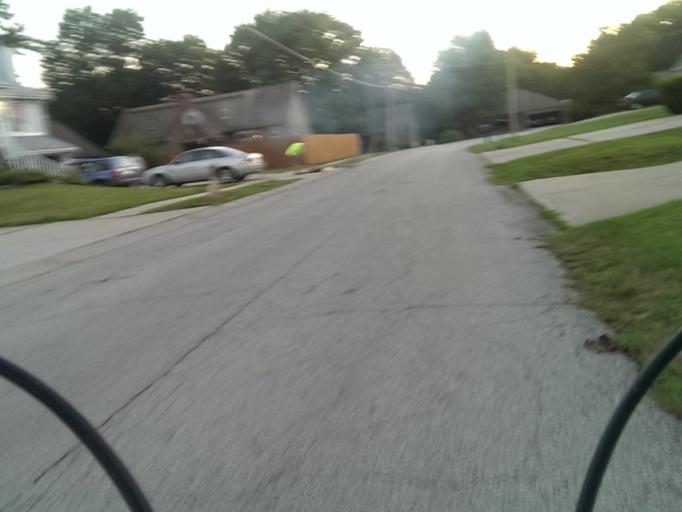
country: US
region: Missouri
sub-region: Jackson County
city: Grandview
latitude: 38.9129
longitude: -94.5787
